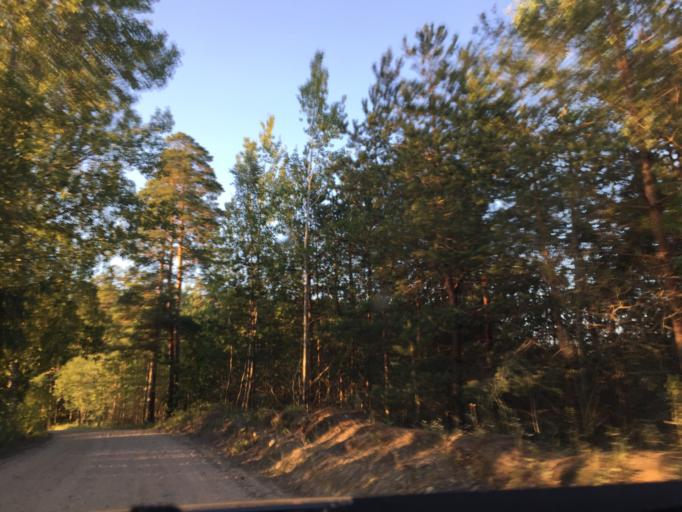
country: LV
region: Koknese
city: Koknese
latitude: 56.6206
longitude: 25.4857
